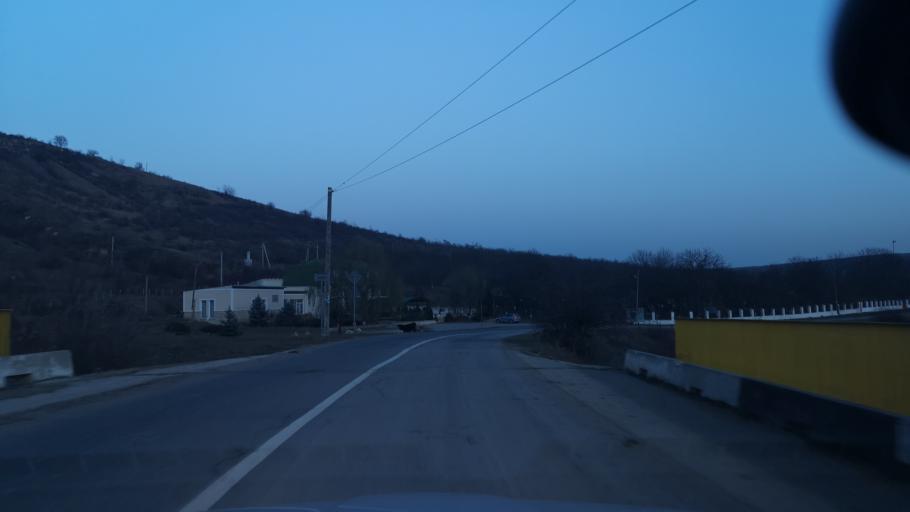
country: MD
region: Telenesti
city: Cocieri
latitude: 47.3076
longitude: 28.9627
